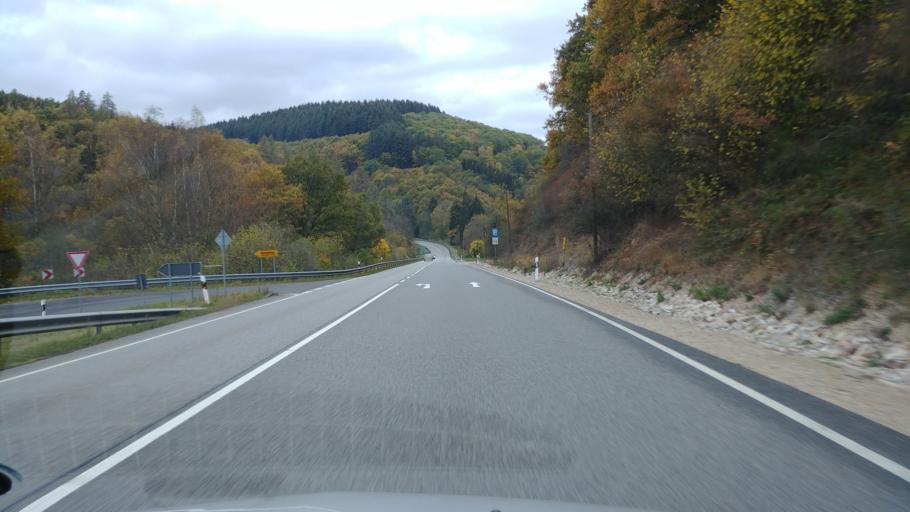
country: DE
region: Rheinland-Pfalz
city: Rorodt
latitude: 49.7811
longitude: 7.0460
